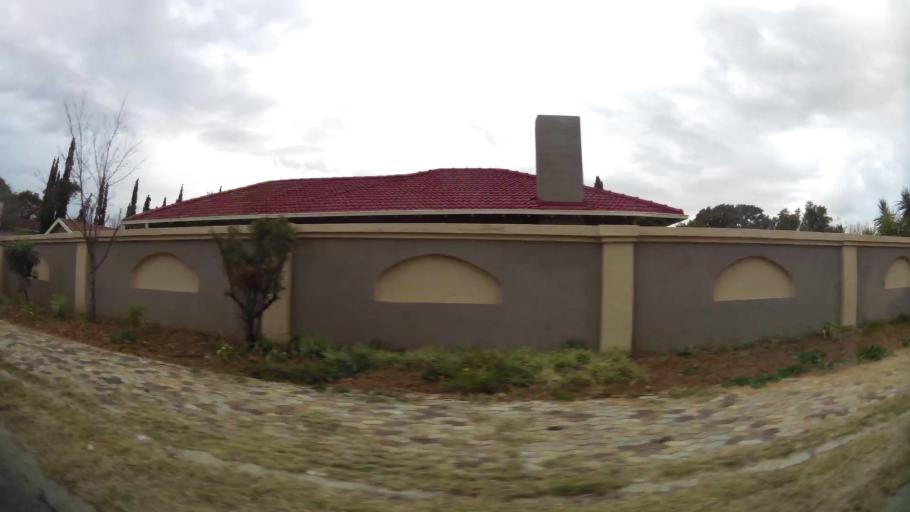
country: ZA
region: Orange Free State
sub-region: Lejweleputswa District Municipality
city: Welkom
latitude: -27.9565
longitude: 26.7252
